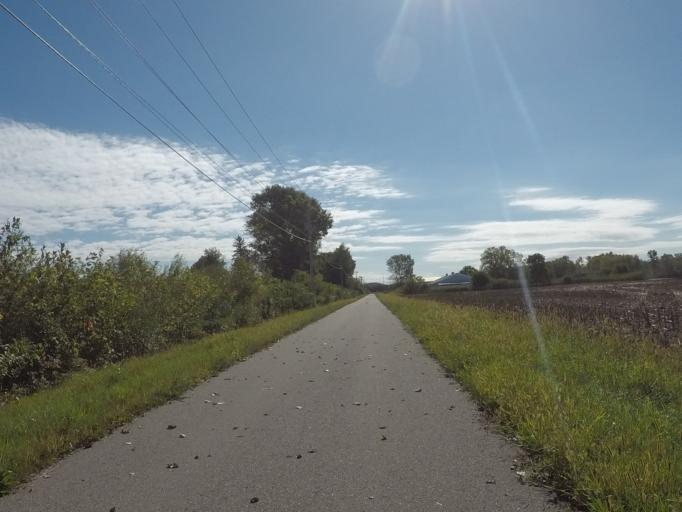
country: US
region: Wisconsin
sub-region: Richland County
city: Richland Center
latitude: 43.3139
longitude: -90.3547
